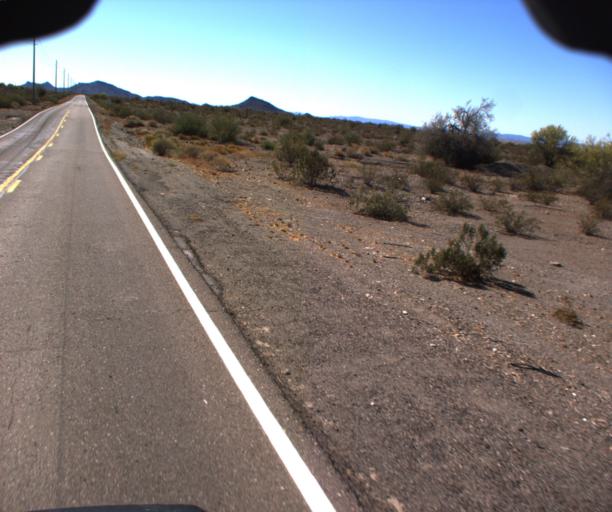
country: US
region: Arizona
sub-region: La Paz County
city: Salome
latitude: 33.7616
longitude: -113.7829
